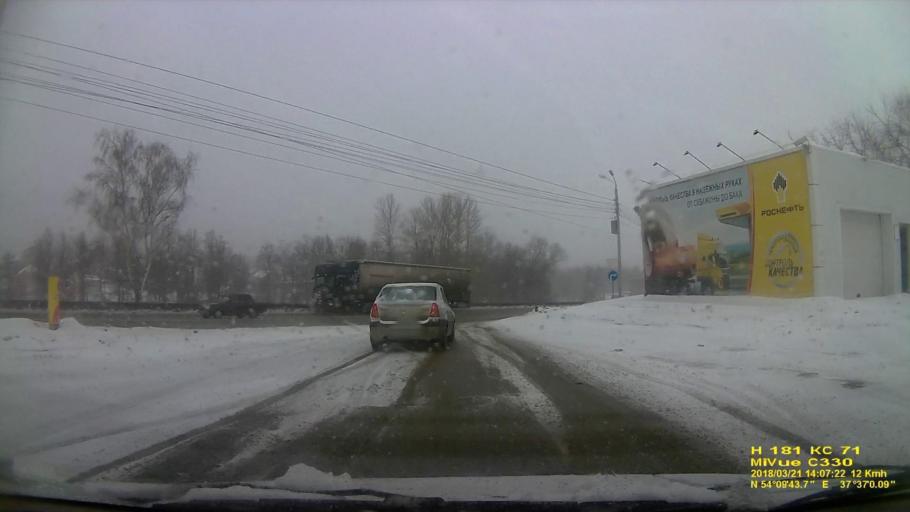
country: RU
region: Tula
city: Tula
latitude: 54.1622
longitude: 37.6167
